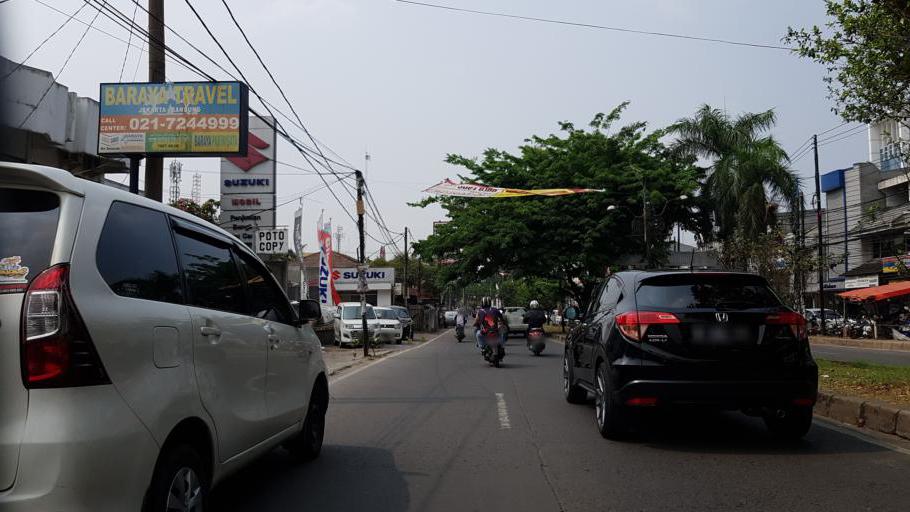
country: ID
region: West Java
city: Pamulang
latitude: -6.3261
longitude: 106.7848
